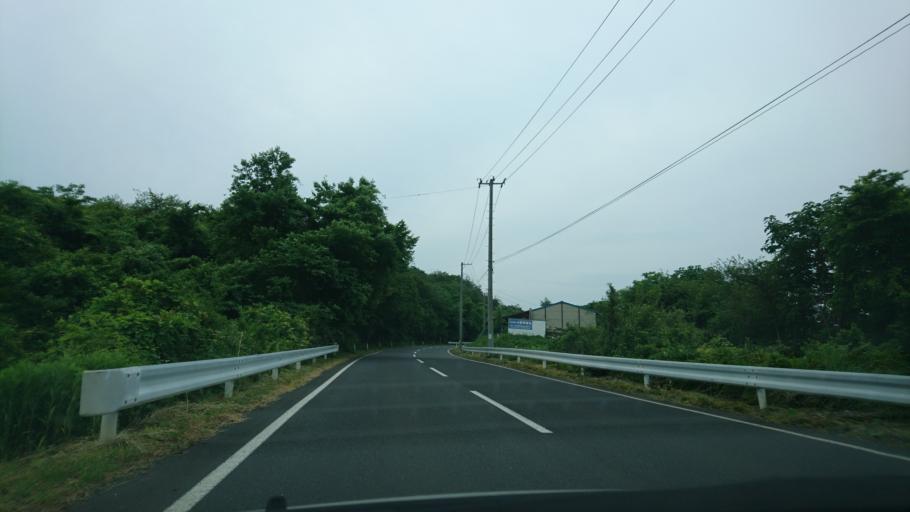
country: JP
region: Iwate
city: Ichinoseki
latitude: 38.8940
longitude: 141.1526
